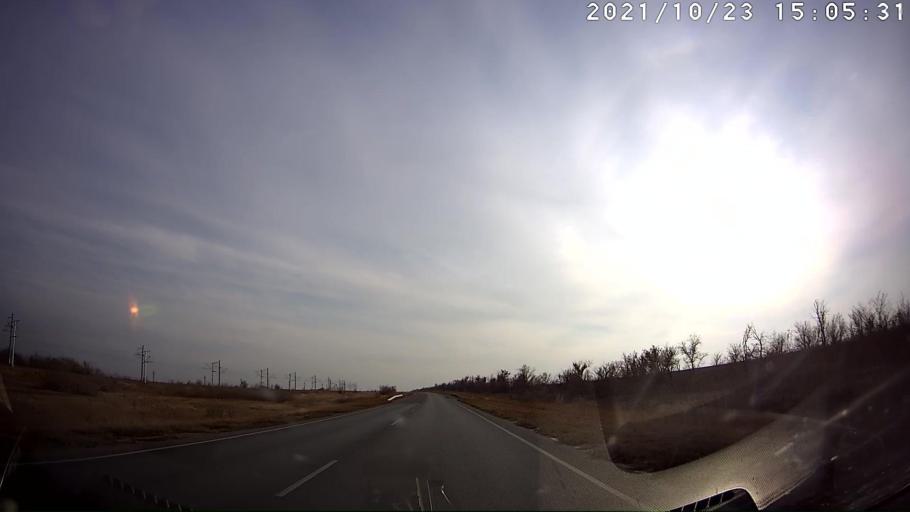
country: RU
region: Volgograd
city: Volgograd
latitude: 48.3836
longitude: 44.3596
